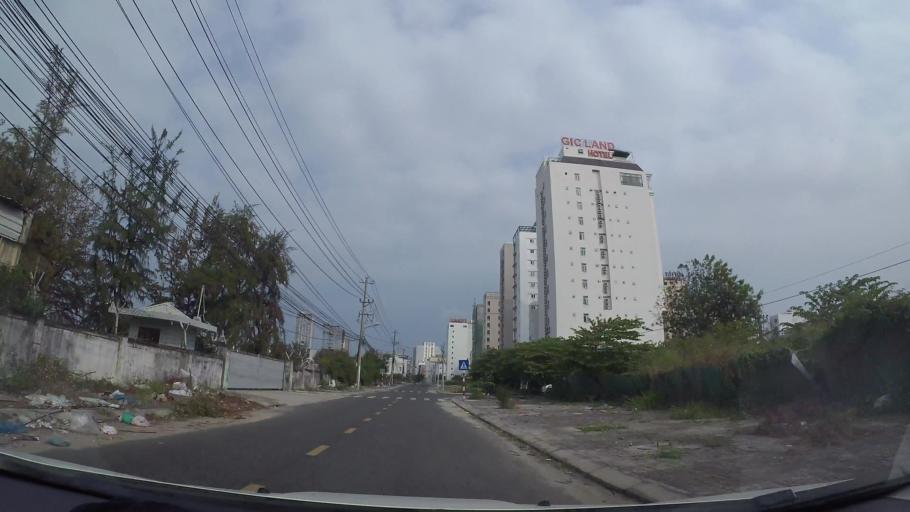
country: VN
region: Da Nang
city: Son Tra
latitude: 16.0724
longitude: 108.2340
